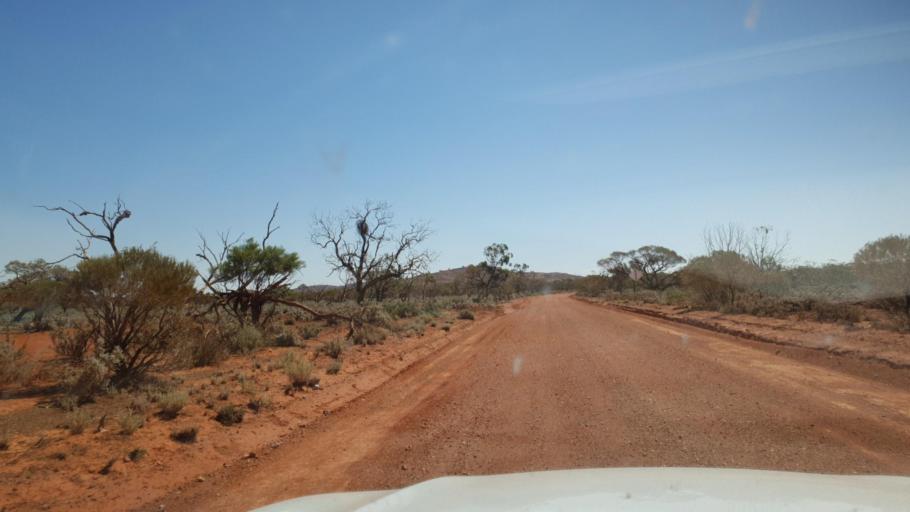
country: AU
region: South Australia
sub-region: Whyalla
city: Whyalla
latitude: -32.6141
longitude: 136.7568
